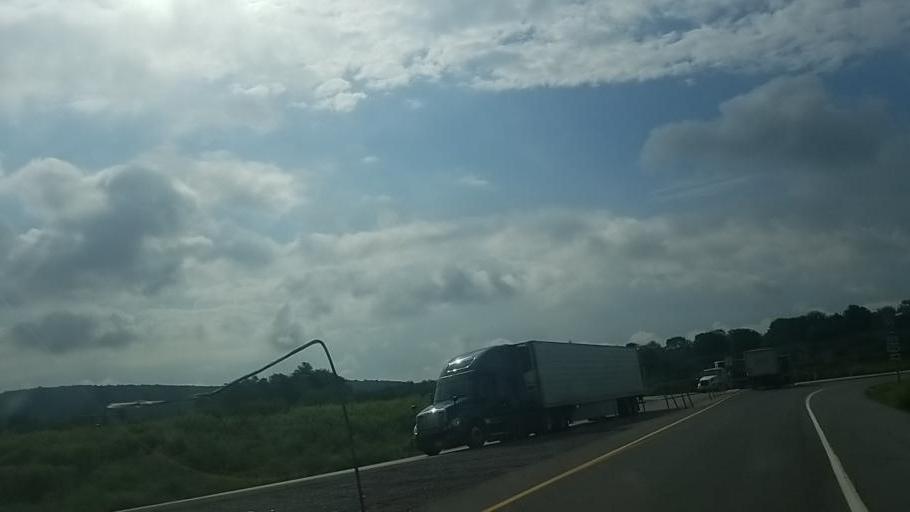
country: US
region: Pennsylvania
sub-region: Centre County
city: Zion
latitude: 40.9429
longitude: -77.7264
